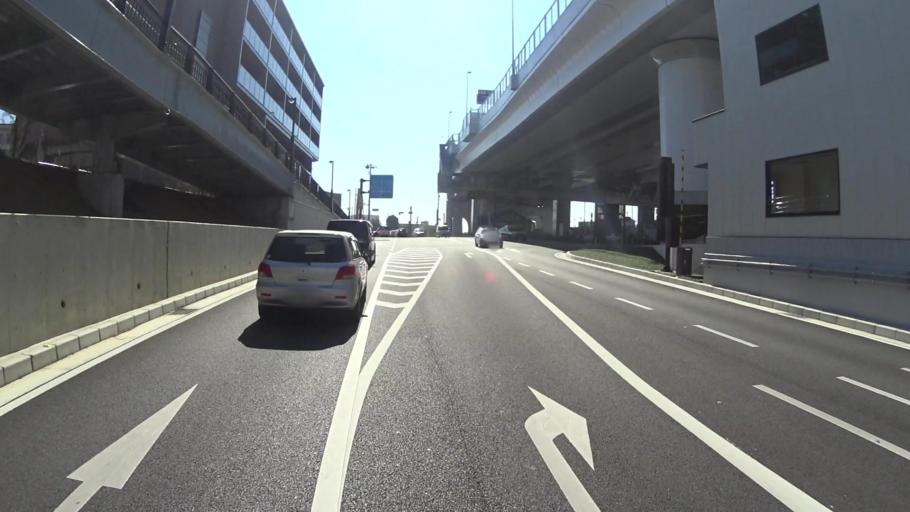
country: JP
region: Kyoto
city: Yawata
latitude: 34.9136
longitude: 135.6887
